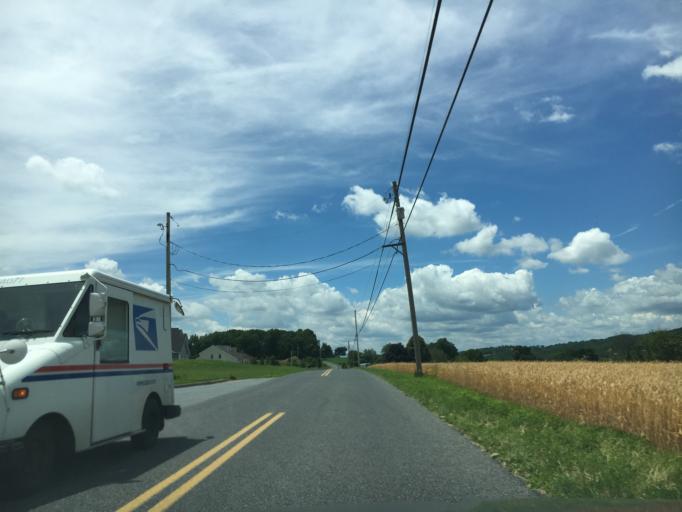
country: US
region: Pennsylvania
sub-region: Lehigh County
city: Laurys Station
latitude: 40.7112
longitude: -75.5584
